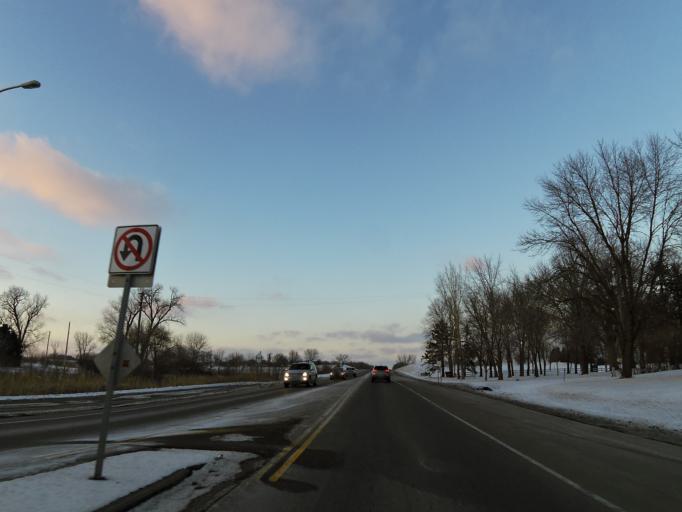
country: US
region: Minnesota
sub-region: Dakota County
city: Farmington
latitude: 44.6747
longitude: -93.1366
